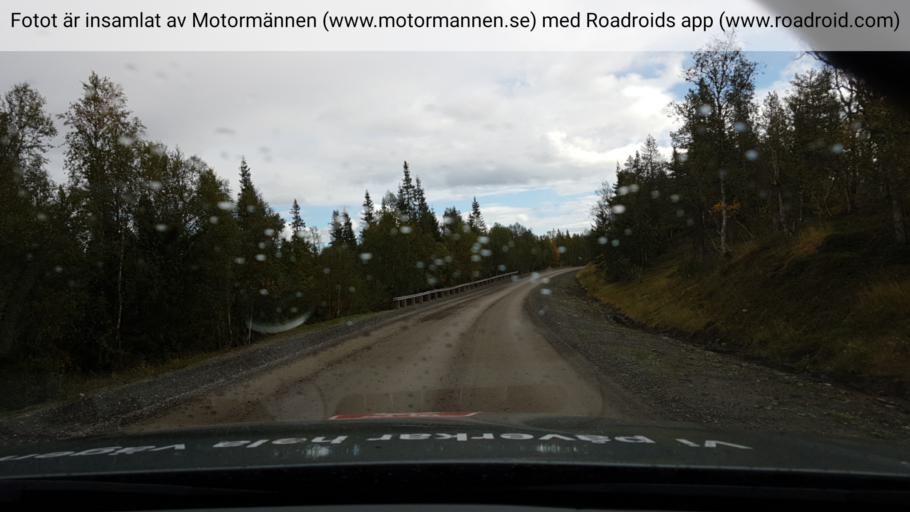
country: NO
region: Nord-Trondelag
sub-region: Snasa
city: Snaase
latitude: 63.7138
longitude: 12.4517
